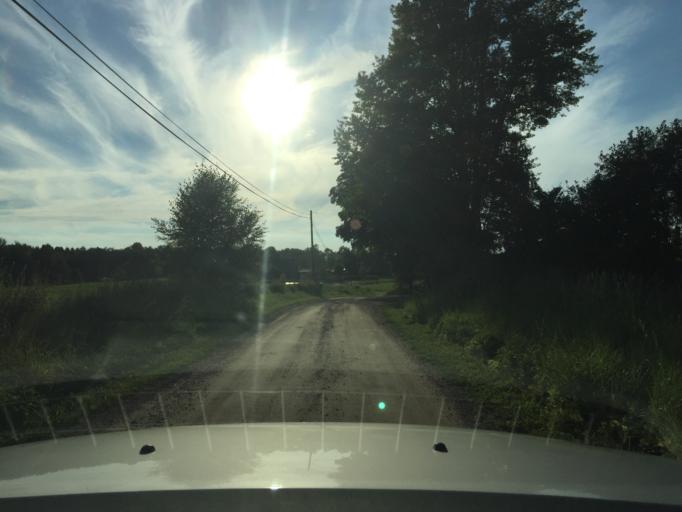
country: SE
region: Skane
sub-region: Hassleholms Kommun
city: Sosdala
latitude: 56.0216
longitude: 13.6990
